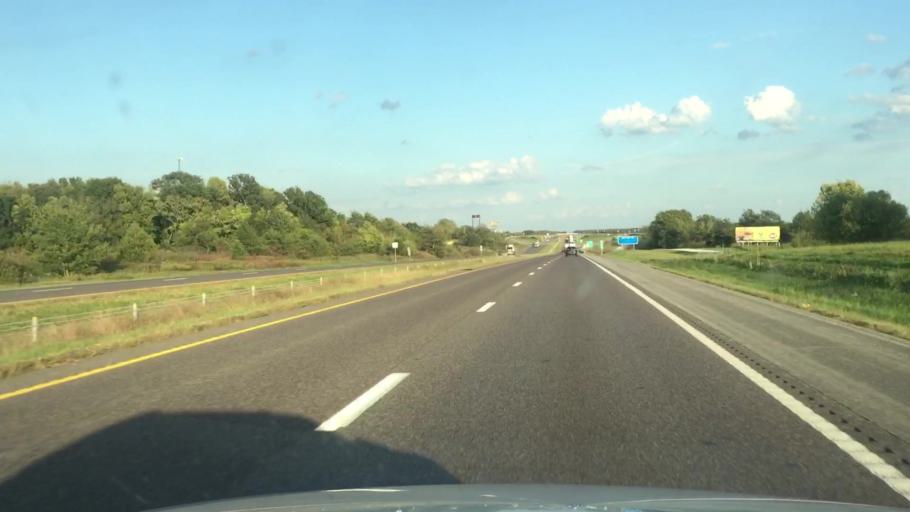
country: US
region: Missouri
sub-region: Saline County
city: Marshall
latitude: 38.9537
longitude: -93.0989
